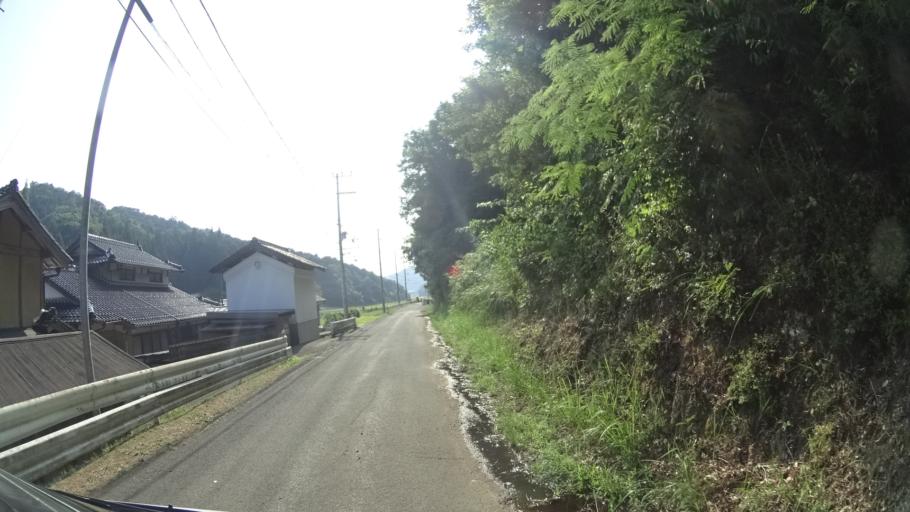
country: JP
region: Kyoto
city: Maizuru
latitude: 35.4337
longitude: 135.2771
